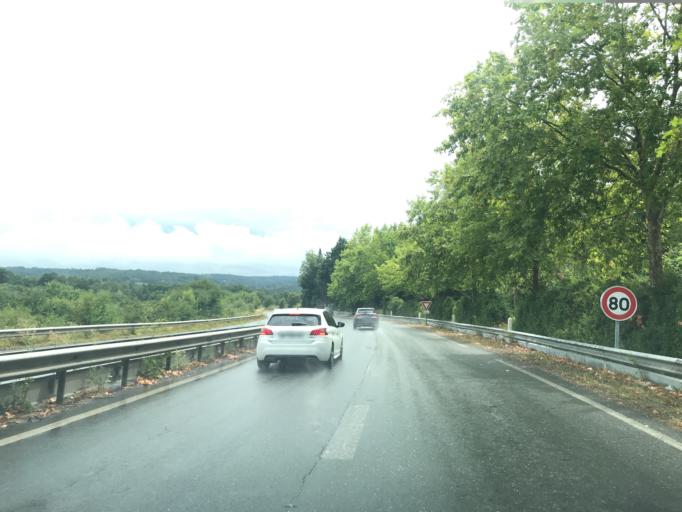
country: FR
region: Aquitaine
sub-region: Departement de la Dordogne
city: Coulounieix-Chamiers
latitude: 45.1530
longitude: 0.7030
